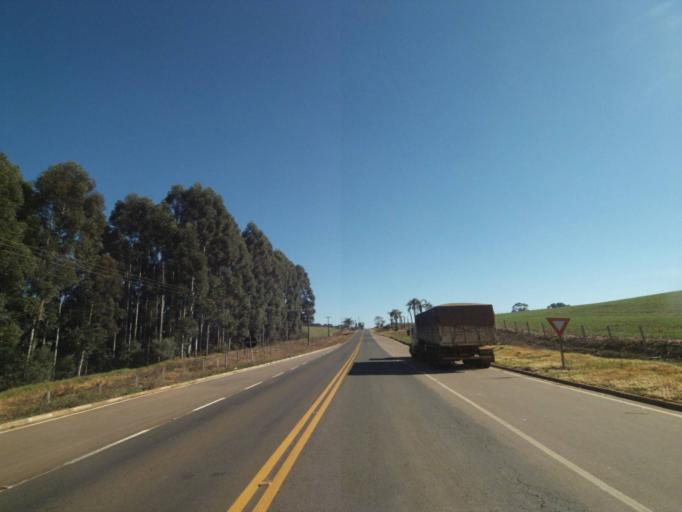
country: BR
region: Parana
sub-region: Tibagi
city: Tibagi
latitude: -24.5098
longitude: -50.4342
